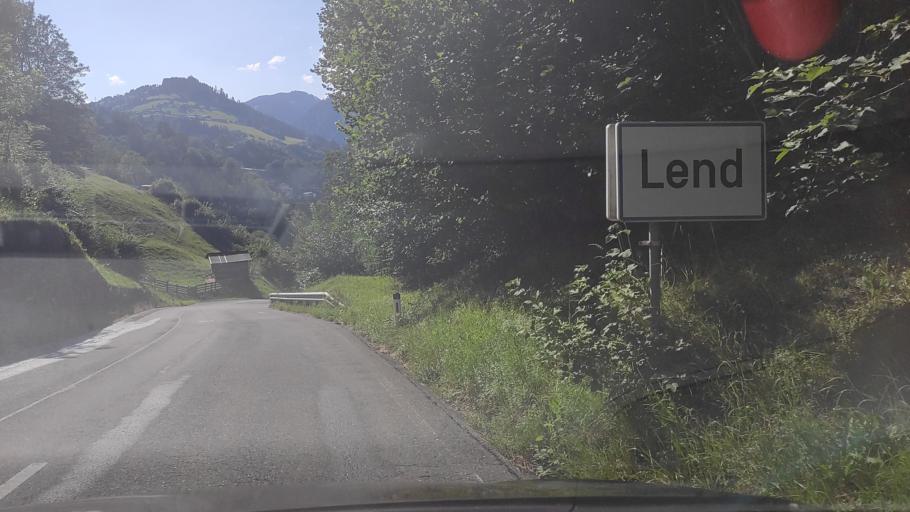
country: AT
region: Salzburg
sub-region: Politischer Bezirk Zell am See
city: Lend
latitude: 47.2952
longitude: 13.0559
